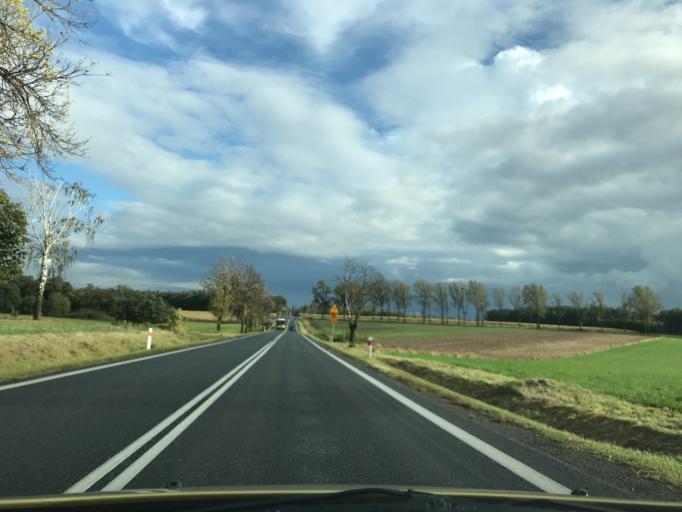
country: PL
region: Greater Poland Voivodeship
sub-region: Powiat ostrowski
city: Nowe Skalmierzyce
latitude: 51.7773
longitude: 18.0183
